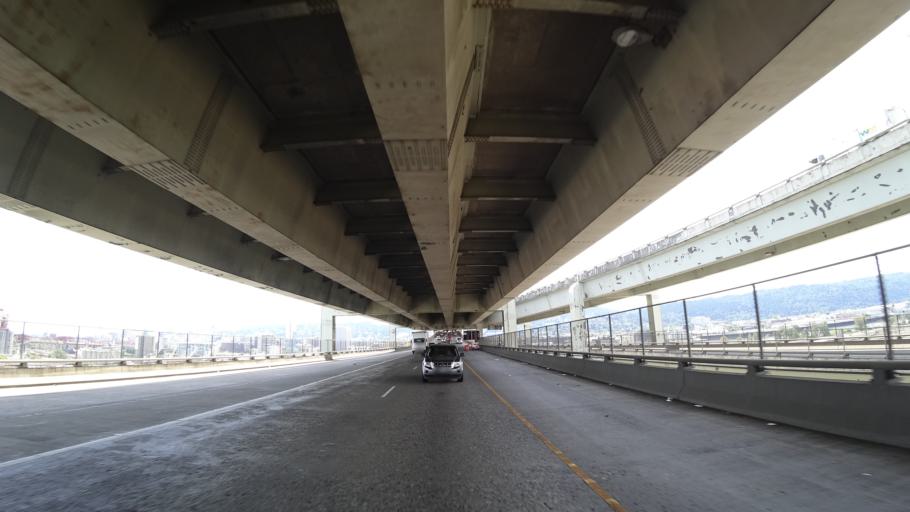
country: US
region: Oregon
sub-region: Multnomah County
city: Portland
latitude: 45.5407
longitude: -122.6817
